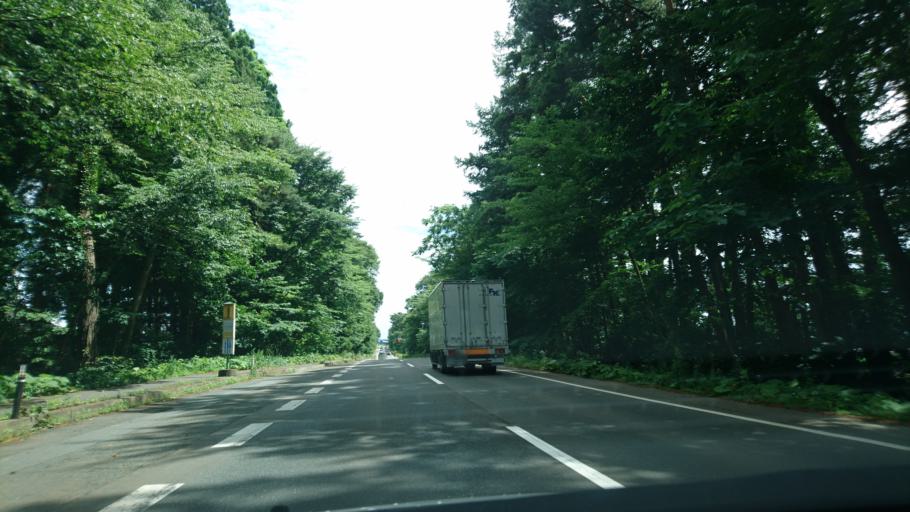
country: JP
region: Iwate
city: Morioka-shi
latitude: 39.7643
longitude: 141.1320
